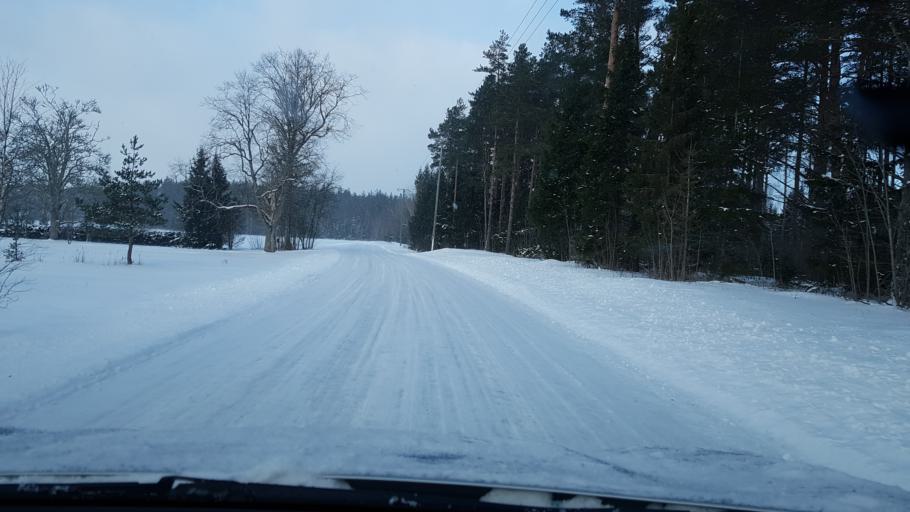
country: EE
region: Harju
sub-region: Nissi vald
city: Turba
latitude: 59.1861
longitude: 24.1407
